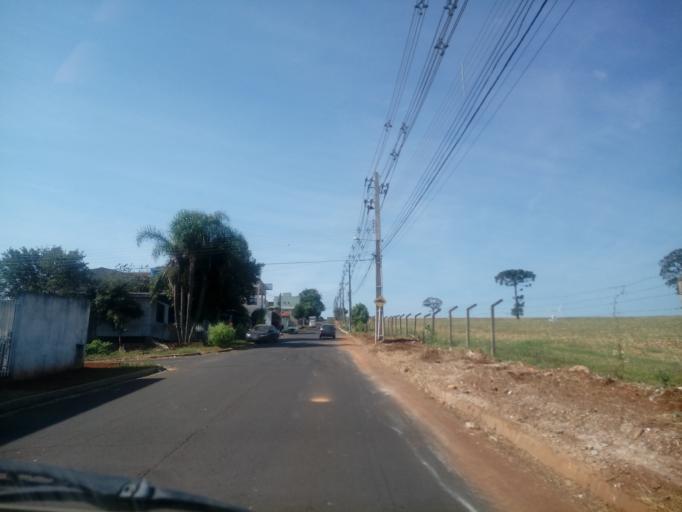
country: BR
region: Santa Catarina
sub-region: Chapeco
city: Chapeco
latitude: -27.0820
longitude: -52.6365
